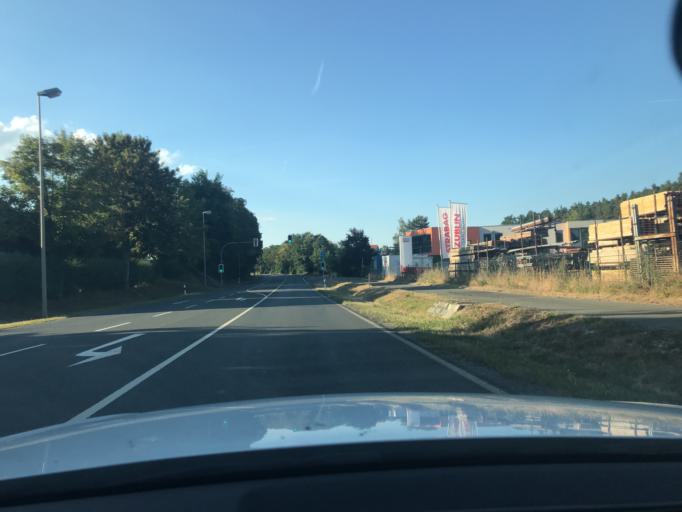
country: DE
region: Bavaria
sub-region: Upper Franconia
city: Emtmannsberg
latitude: 49.9050
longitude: 11.6084
